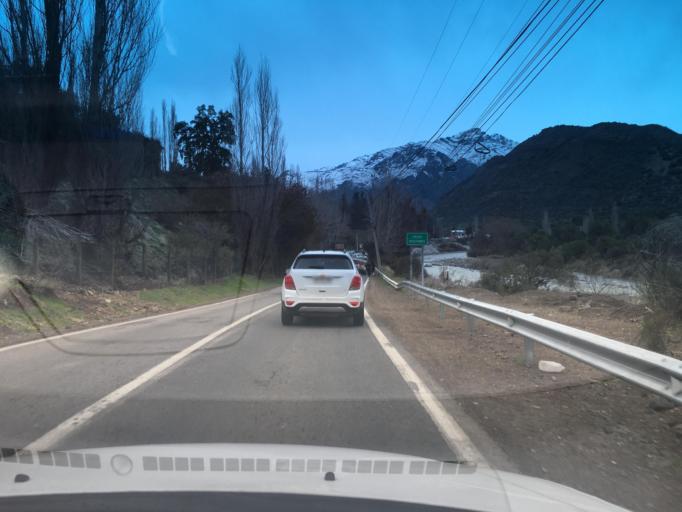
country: CL
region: Santiago Metropolitan
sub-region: Provincia de Cordillera
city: Puente Alto
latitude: -33.6799
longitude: -70.3390
